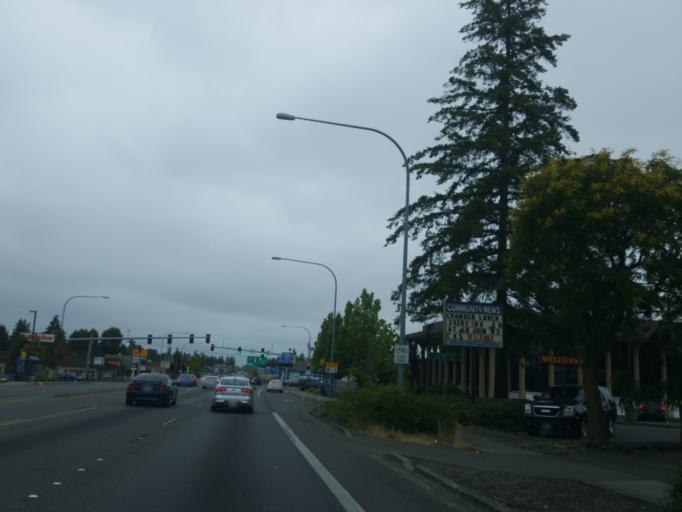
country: US
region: Washington
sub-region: Pierce County
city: Parkland
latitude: 47.1542
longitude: -122.4342
